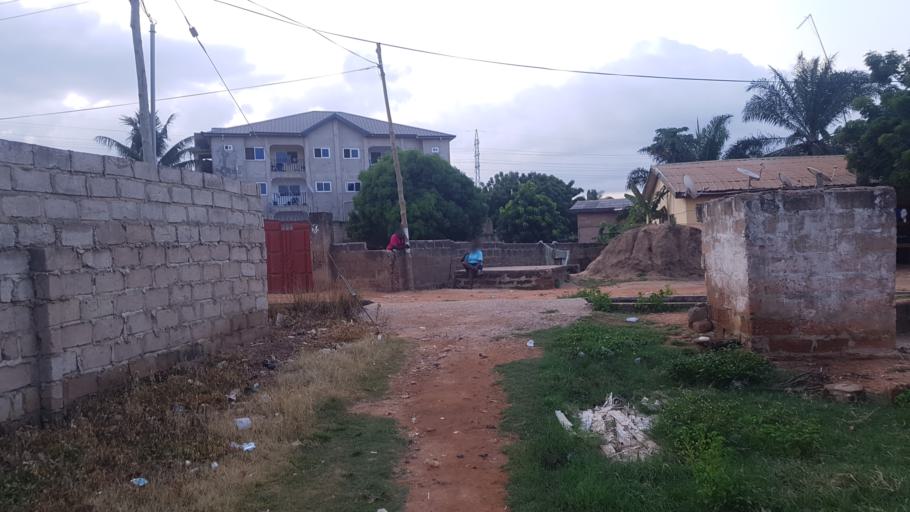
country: GH
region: Greater Accra
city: Gbawe
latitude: 5.5531
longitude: -0.3498
